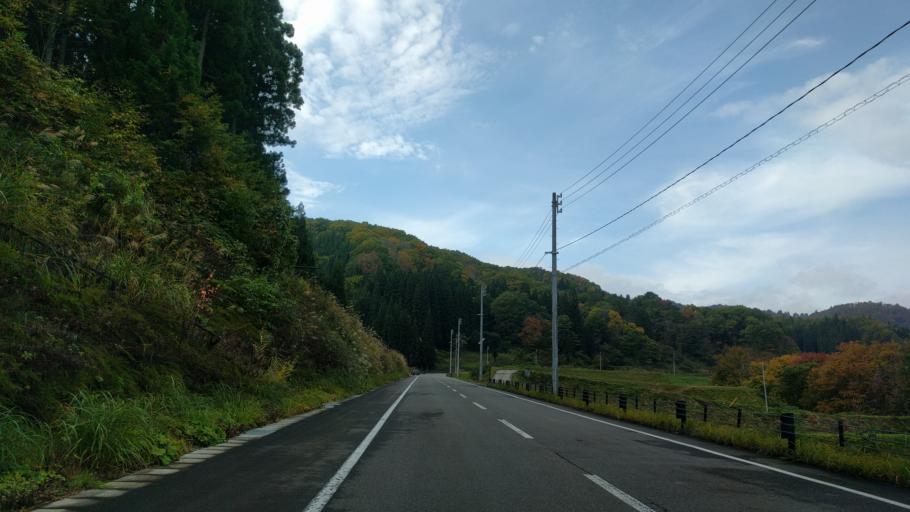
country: JP
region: Fukushima
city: Kitakata
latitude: 37.3969
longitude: 139.6929
